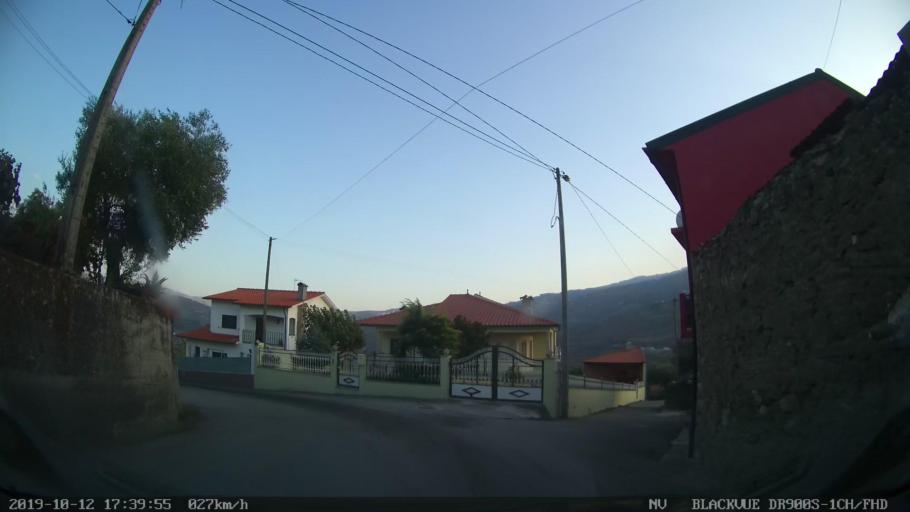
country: PT
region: Vila Real
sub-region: Peso da Regua
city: Godim
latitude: 41.1547
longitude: -7.8184
